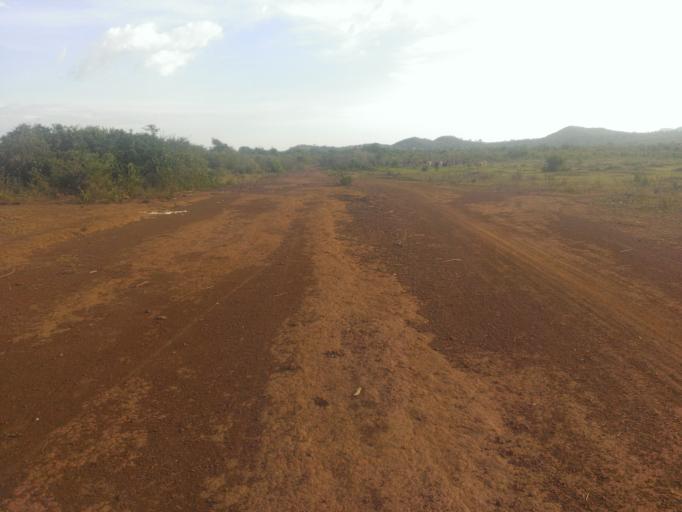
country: UG
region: Eastern Region
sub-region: Busia District
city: Busia
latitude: 0.5462
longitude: 33.9846
